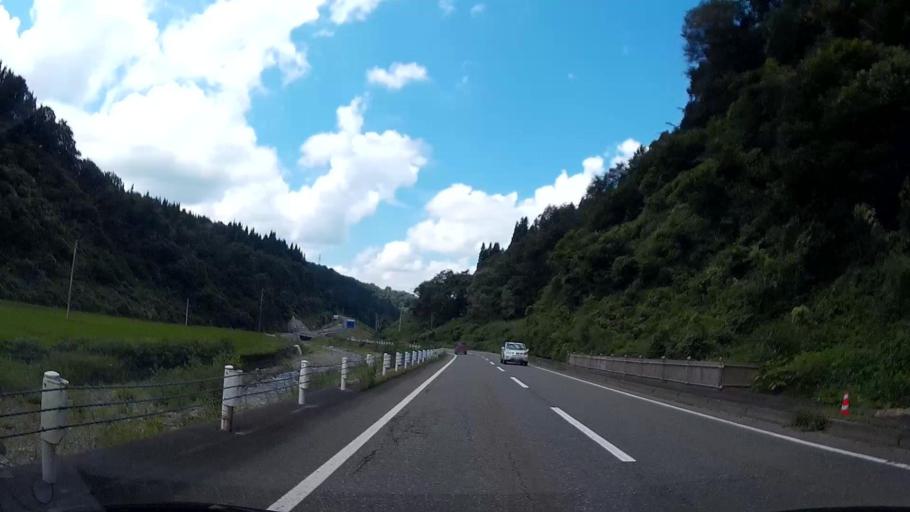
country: JP
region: Niigata
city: Shiozawa
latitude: 37.0474
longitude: 138.7696
